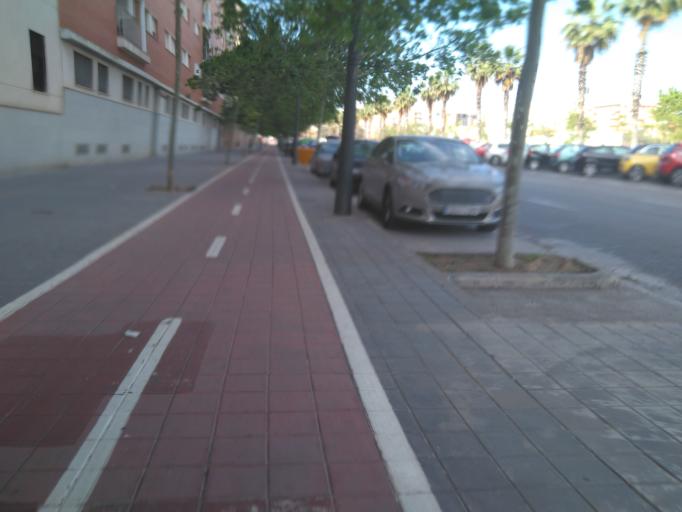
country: ES
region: Valencia
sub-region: Provincia de Valencia
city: Tavernes Blanques
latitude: 39.4957
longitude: -0.3886
